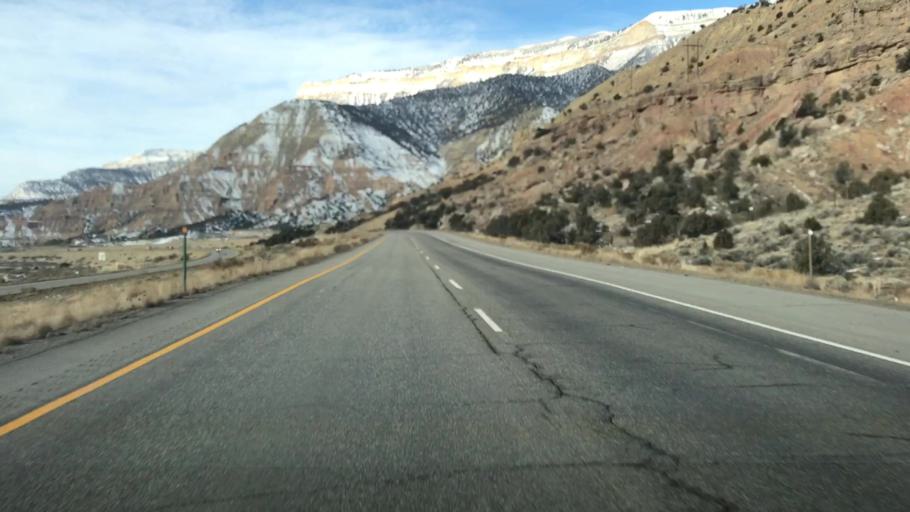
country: US
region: Colorado
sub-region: Garfield County
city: Battlement Mesa
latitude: 39.5004
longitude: -107.9267
